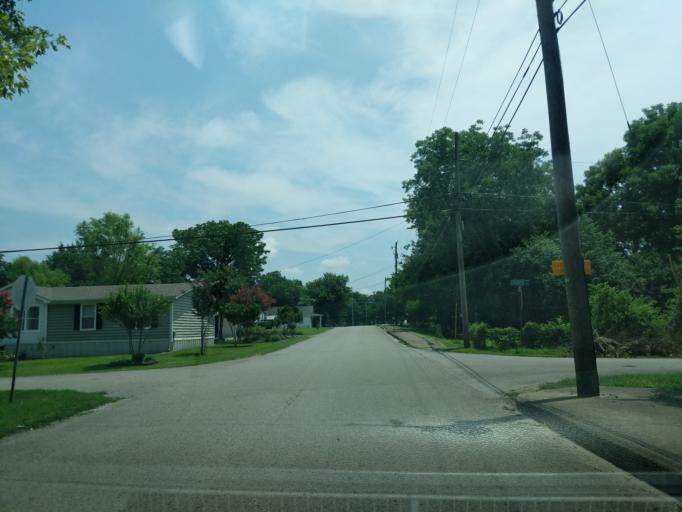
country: US
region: Tennessee
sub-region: Davidson County
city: Lakewood
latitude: 36.2255
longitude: -86.6283
